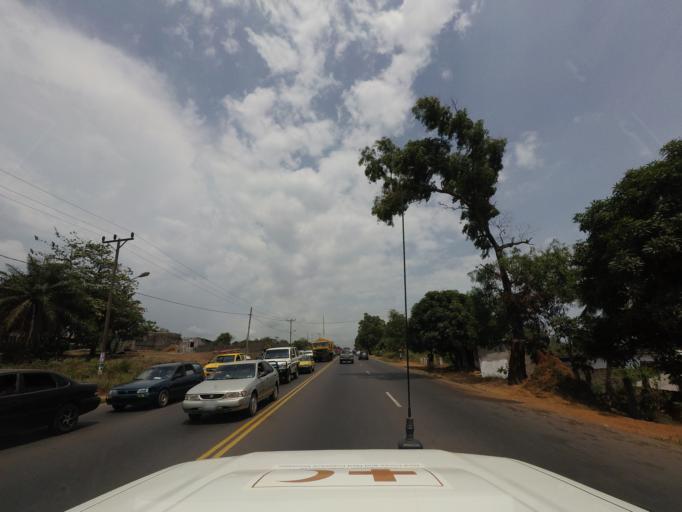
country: LR
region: Montserrado
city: Monrovia
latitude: 6.2691
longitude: -10.7309
